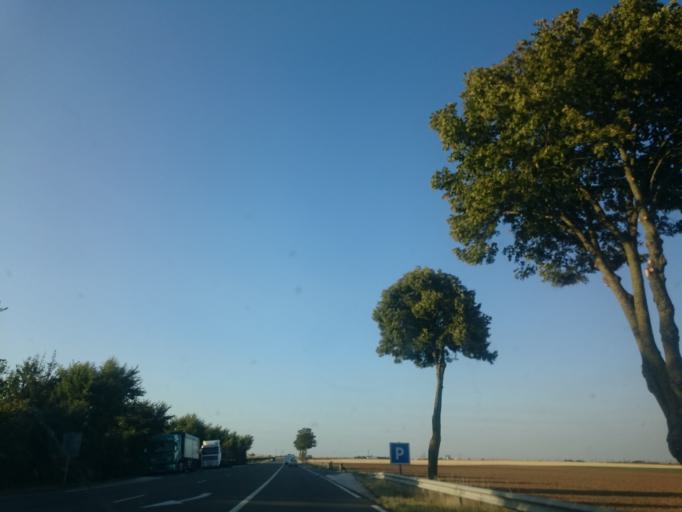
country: FR
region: Centre
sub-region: Departement d'Eure-et-Loir
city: Toury
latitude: 48.2389
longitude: 1.9556
